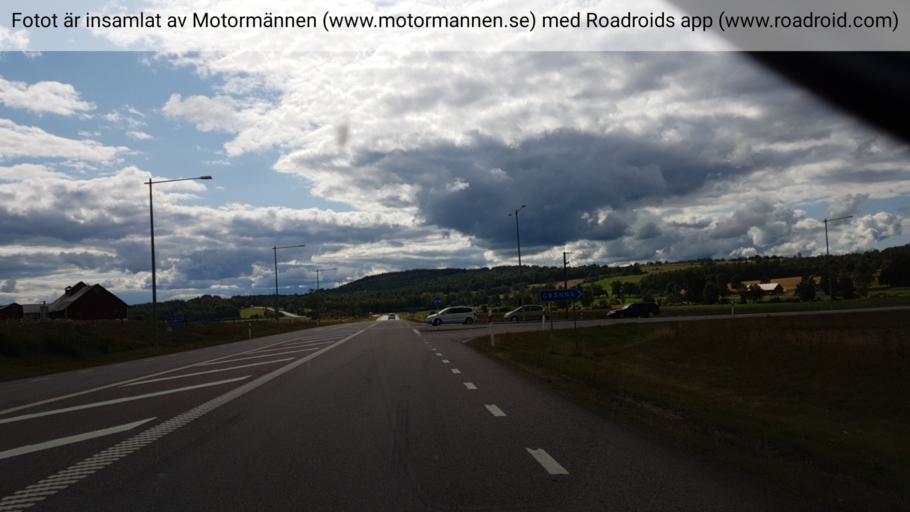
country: SE
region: Joenkoeping
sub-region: Tranas Kommun
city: Tranas
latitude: 57.9922
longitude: 14.9187
